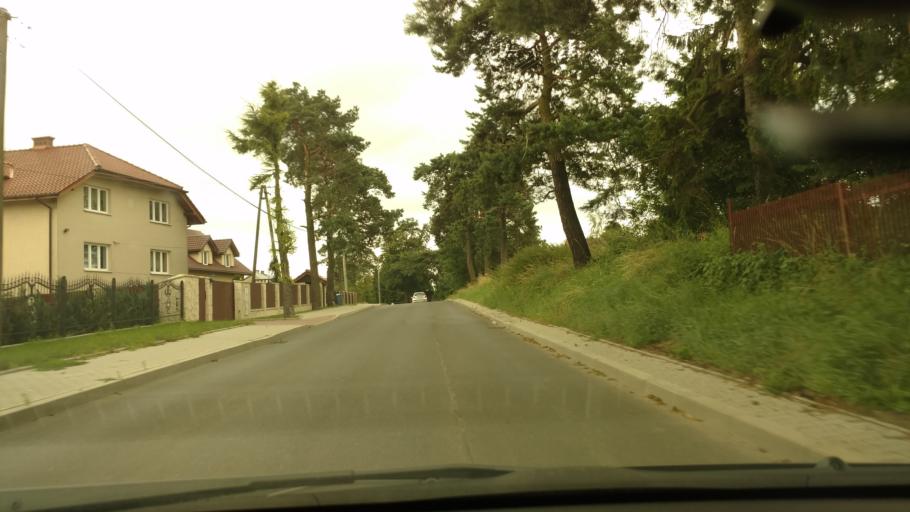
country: PL
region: Lesser Poland Voivodeship
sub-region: Powiat krakowski
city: Zielonki
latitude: 50.1221
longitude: 19.9399
